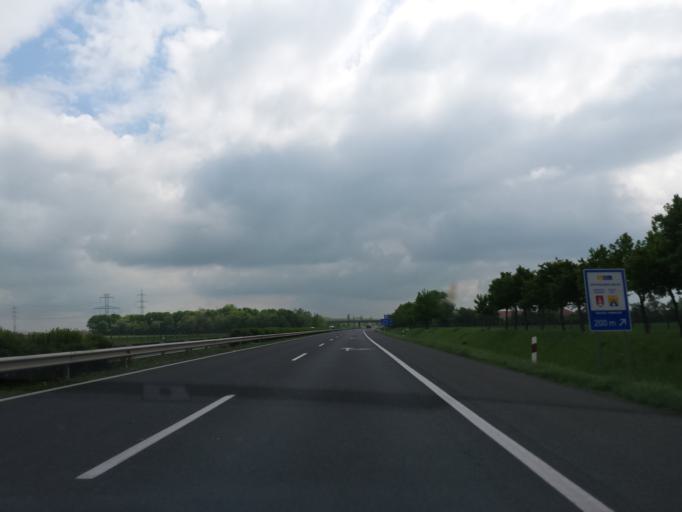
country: HU
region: Gyor-Moson-Sopron
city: Lebeny
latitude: 47.7551
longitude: 17.4086
